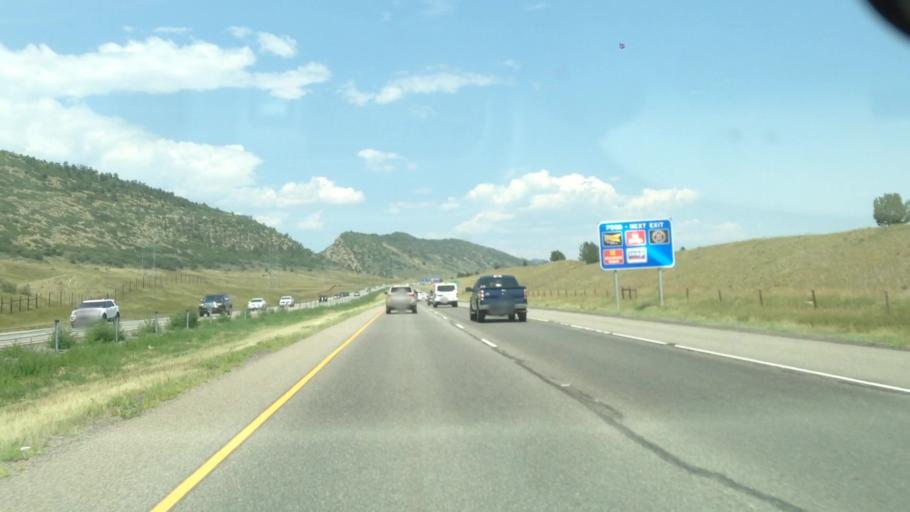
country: US
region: Colorado
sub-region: Jefferson County
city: Ken Caryl
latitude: 39.5669
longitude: -105.1309
